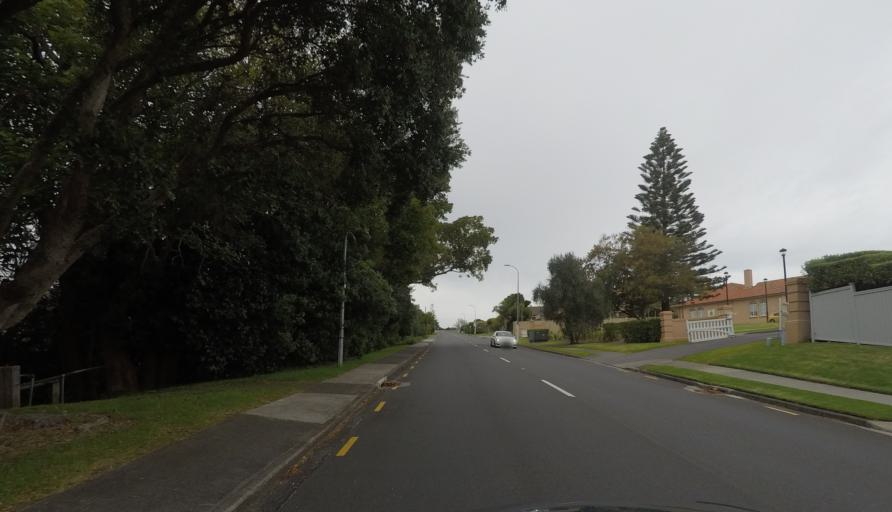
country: NZ
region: Auckland
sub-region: Auckland
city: Pakuranga
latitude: -36.8942
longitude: 174.9429
